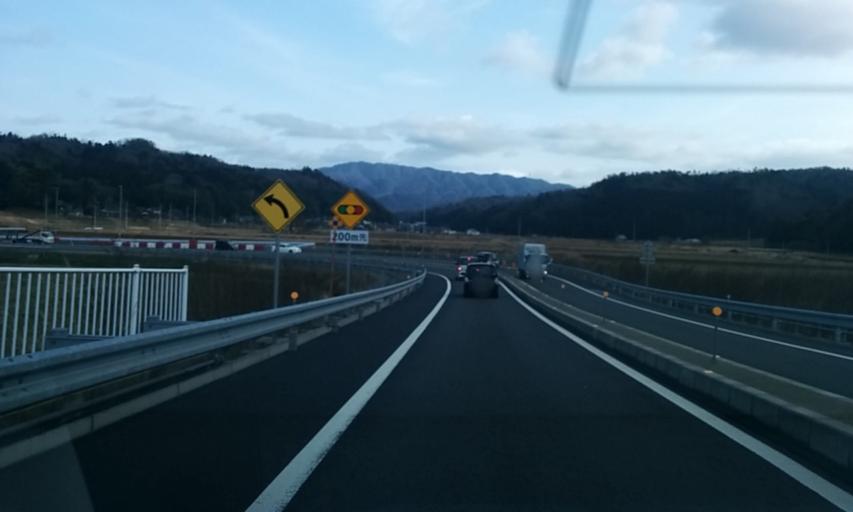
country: JP
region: Kyoto
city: Miyazu
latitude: 35.5761
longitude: 135.1217
